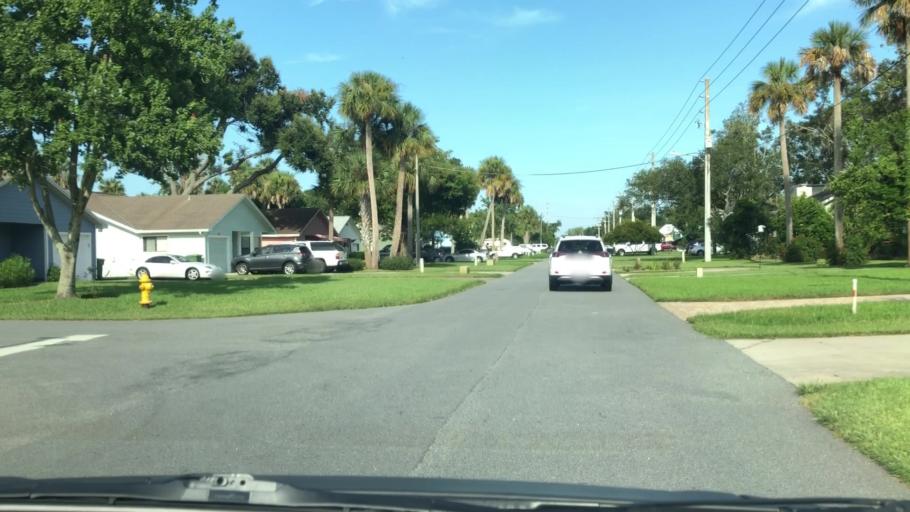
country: US
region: Florida
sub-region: Duval County
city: Jacksonville Beach
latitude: 30.2898
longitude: -81.4042
